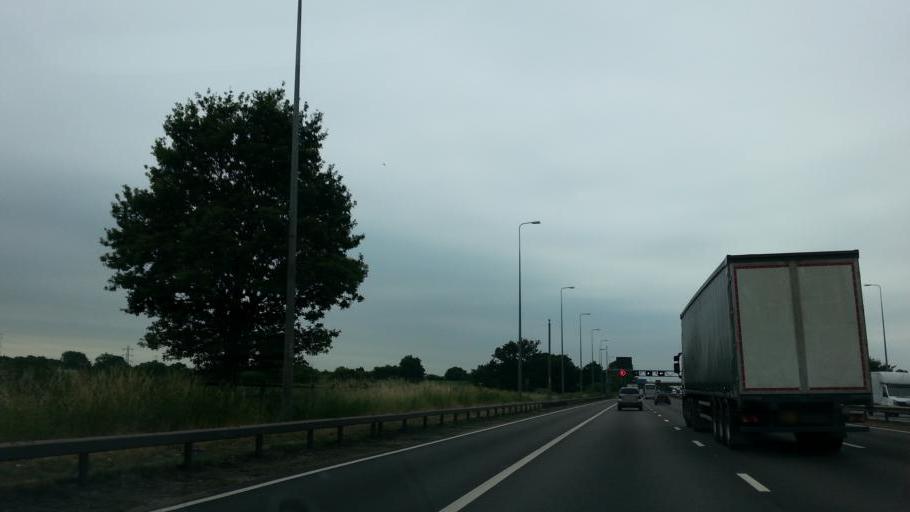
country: GB
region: England
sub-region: Solihull
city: Bickenhill
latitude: 52.4194
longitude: -1.7228
